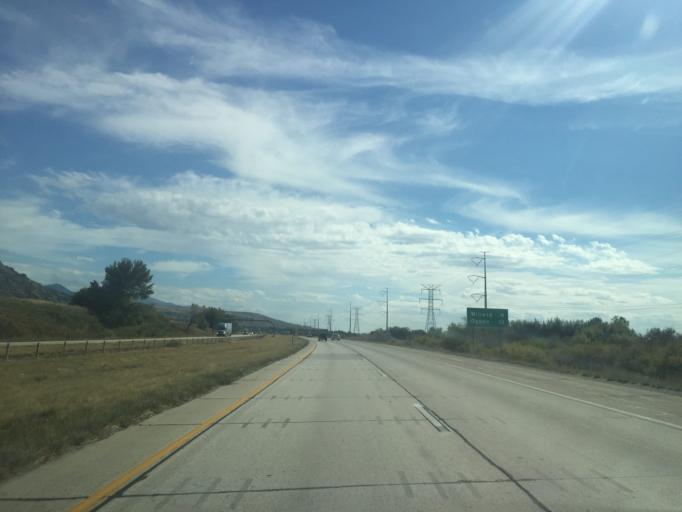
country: US
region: Utah
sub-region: Box Elder County
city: Willard
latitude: 41.4084
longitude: -112.0500
